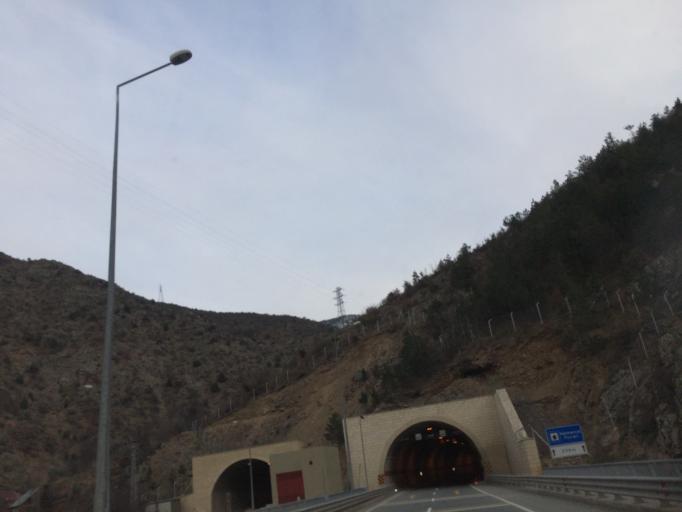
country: TR
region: Gumushane
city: Torul
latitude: 40.5480
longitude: 39.3195
